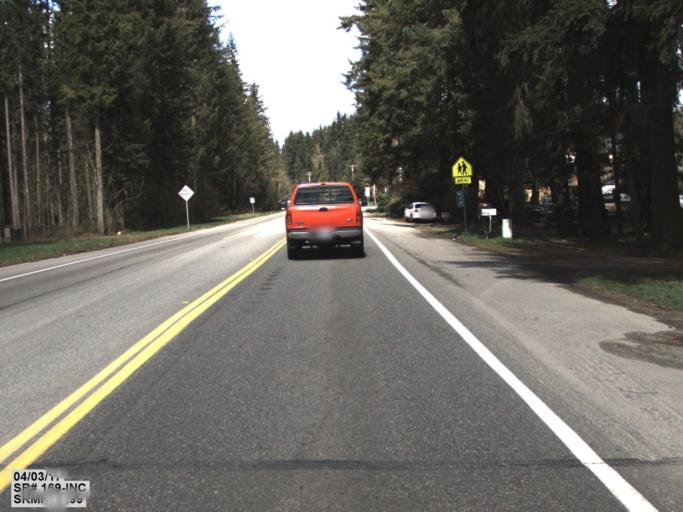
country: US
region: Washington
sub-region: King County
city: Maple Valley
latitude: 47.3693
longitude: -122.0226
